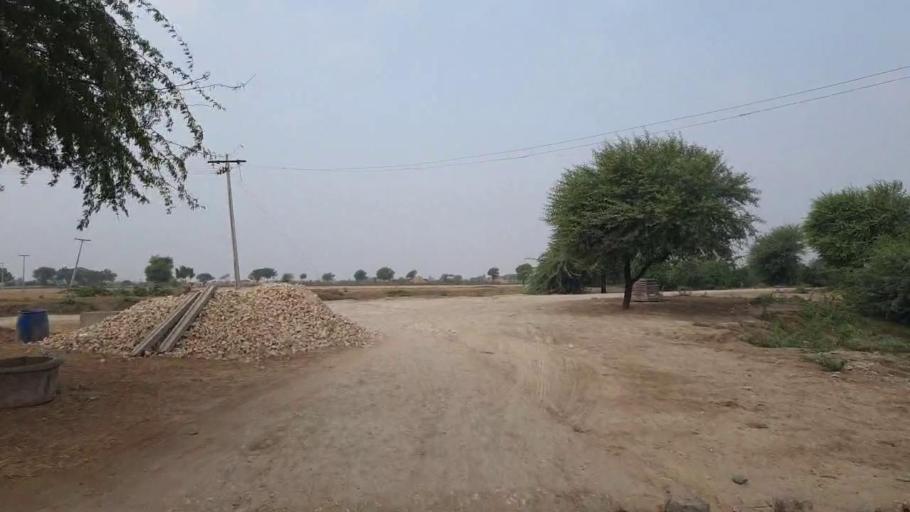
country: PK
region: Sindh
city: Kario
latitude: 24.8743
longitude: 68.5168
